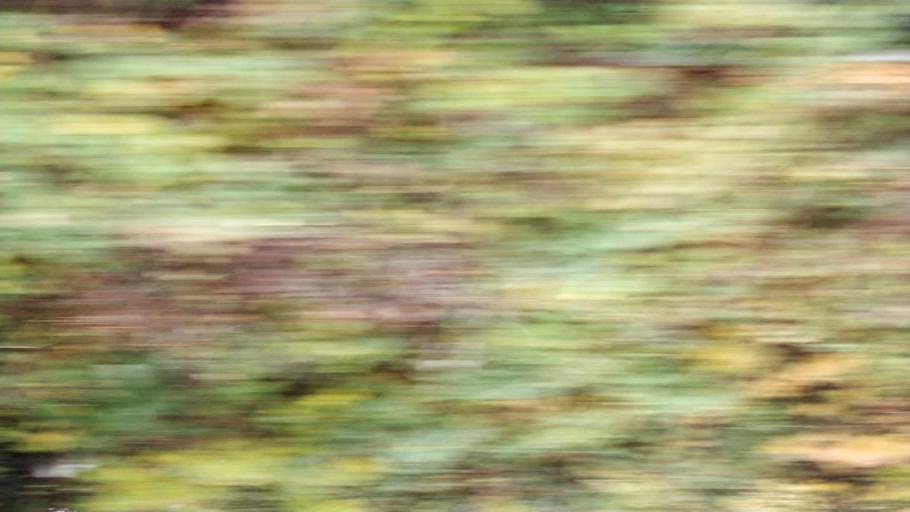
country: GB
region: England
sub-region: City and Borough of Salford
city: Salford
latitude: 53.4920
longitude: -2.2825
